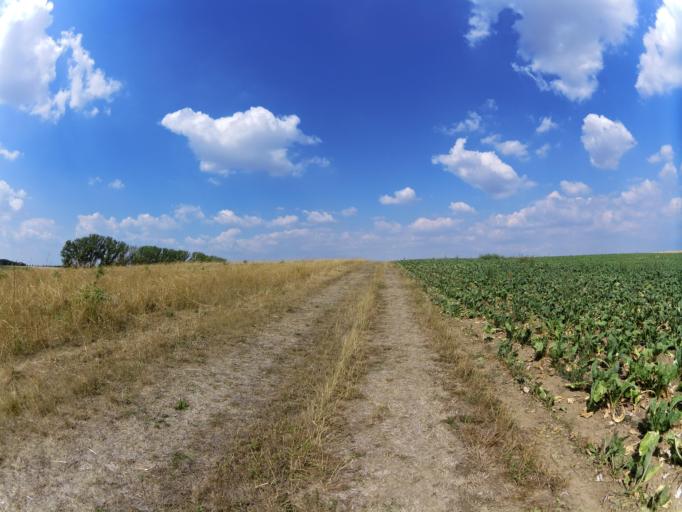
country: DE
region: Bavaria
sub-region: Regierungsbezirk Unterfranken
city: Ochsenfurt
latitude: 49.6436
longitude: 10.0609
